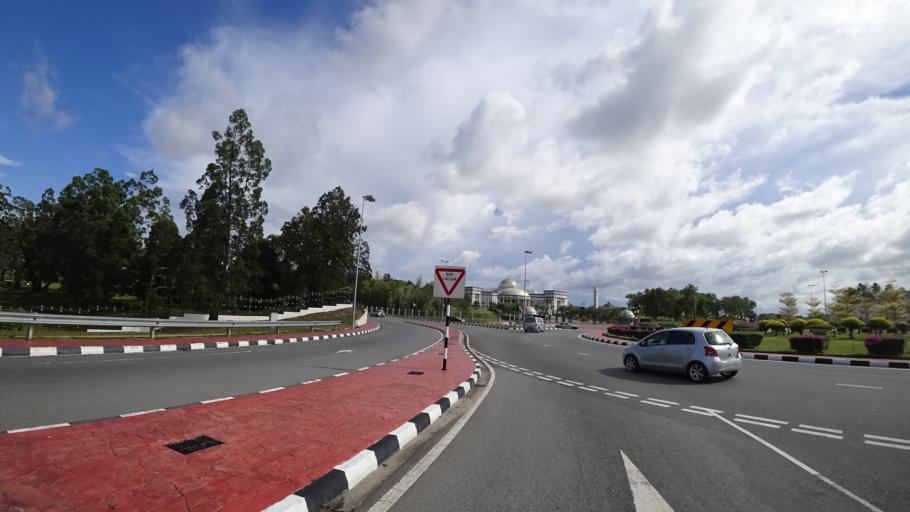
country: BN
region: Brunei and Muara
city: Bandar Seri Begawan
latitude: 4.9242
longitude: 114.9371
